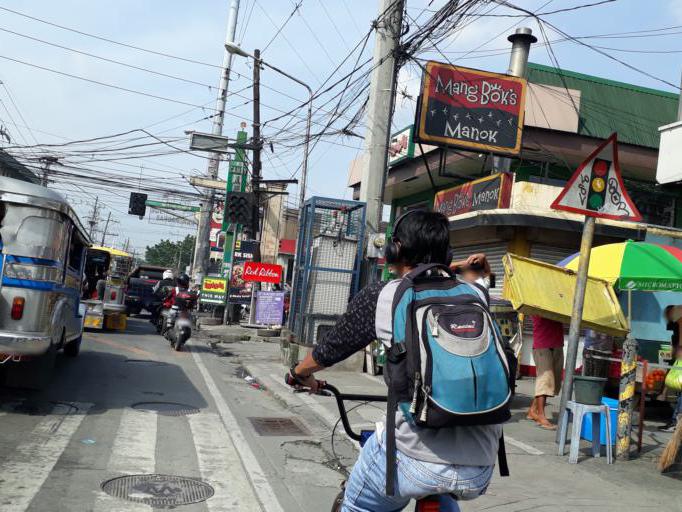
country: PH
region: Calabarzon
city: Bagong Pagasa
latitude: 14.6800
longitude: 121.0186
